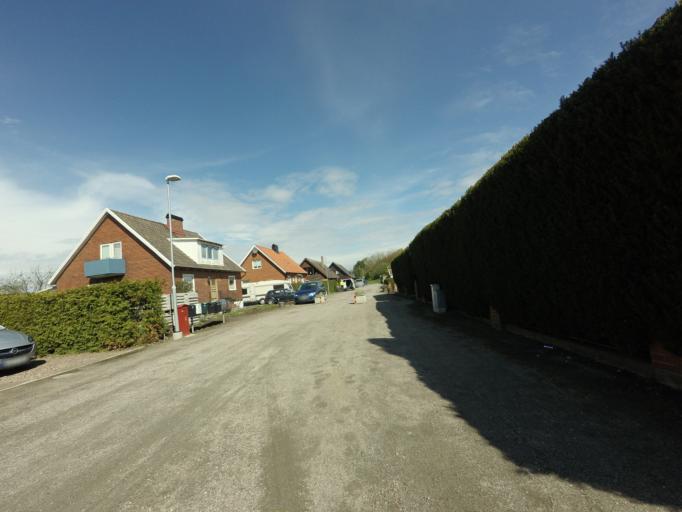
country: SE
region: Skane
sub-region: Malmo
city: Tygelsjo
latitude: 55.4945
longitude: 13.0015
